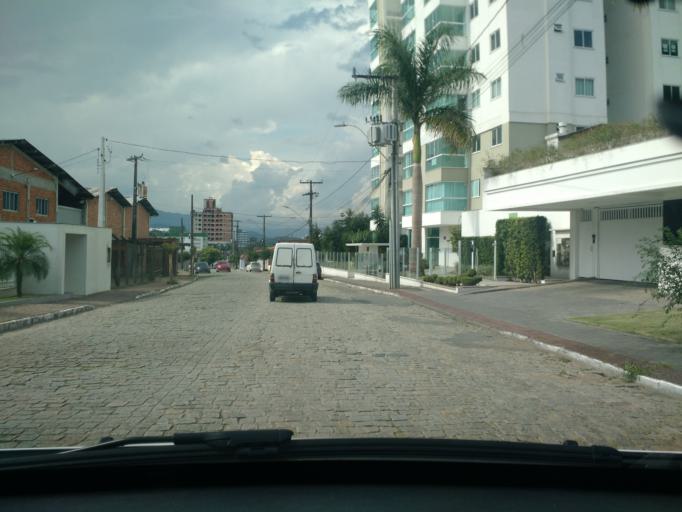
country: BR
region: Santa Catarina
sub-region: Jaragua Do Sul
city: Jaragua do Sul
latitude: -26.5058
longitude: -49.0866
